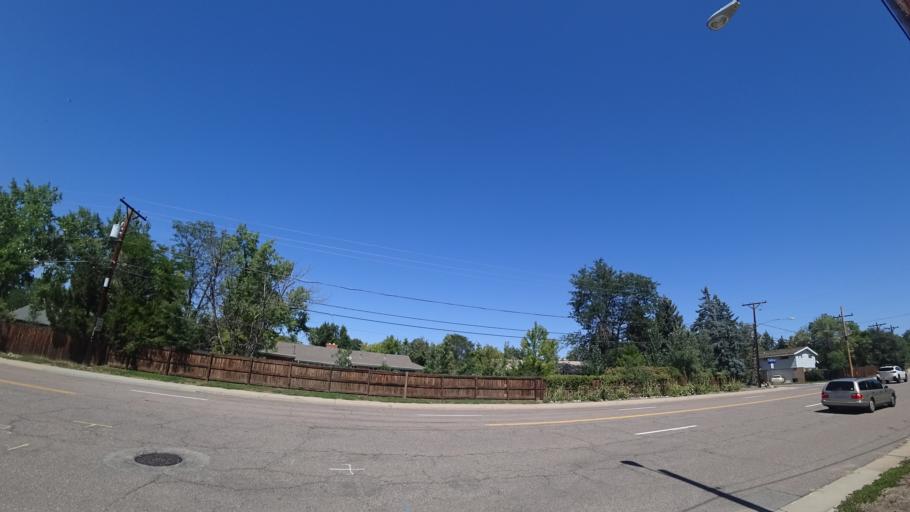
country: US
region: Colorado
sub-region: Arapahoe County
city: Greenwood Village
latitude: 39.6095
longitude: -104.9821
